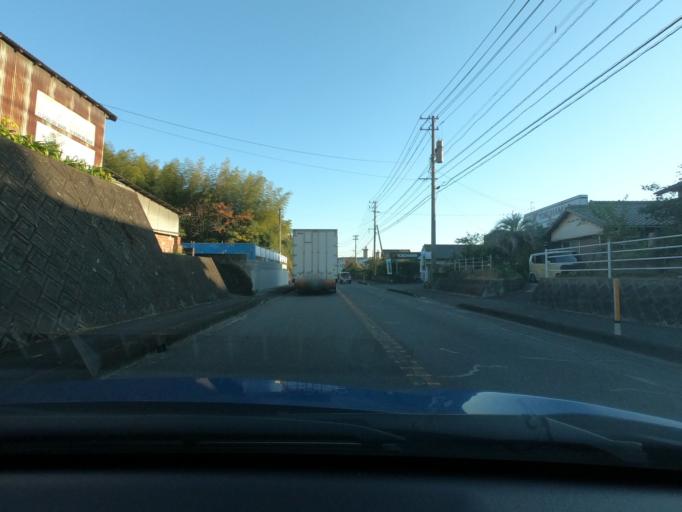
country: JP
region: Kagoshima
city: Satsumasendai
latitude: 31.8399
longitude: 130.2829
